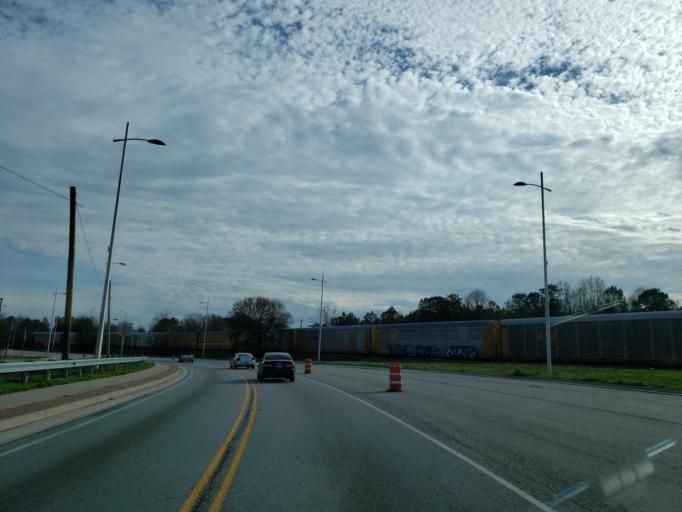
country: US
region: Georgia
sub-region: Clayton County
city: Forest Park
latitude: 33.6358
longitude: -84.3900
